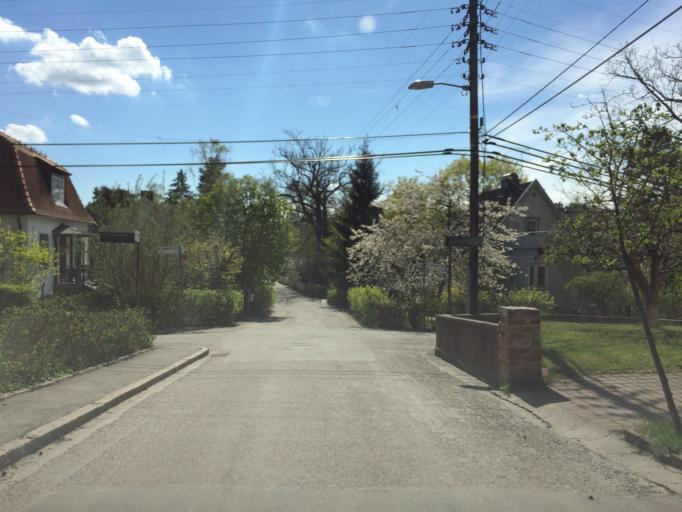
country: SE
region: Stockholm
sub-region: Huddinge Kommun
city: Segeltorp
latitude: 59.3020
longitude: 17.9620
